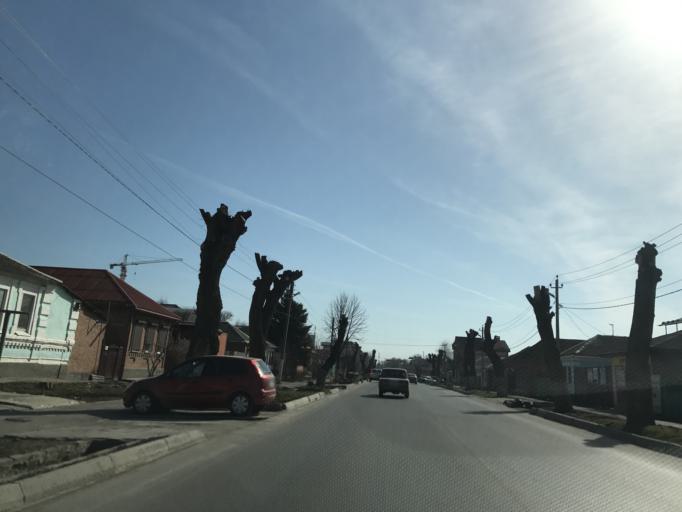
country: RU
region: Rostov
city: Bataysk
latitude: 47.1439
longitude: 39.7389
